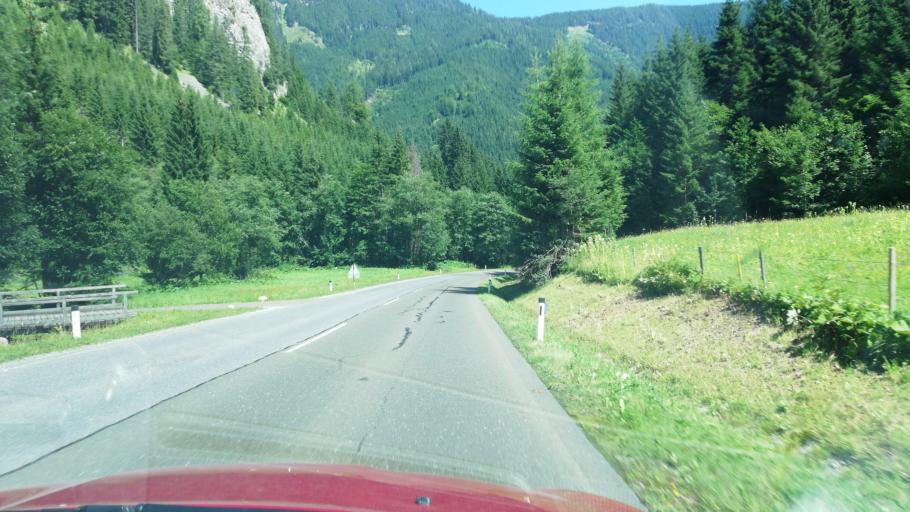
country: AT
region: Styria
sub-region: Politischer Bezirk Murtal
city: Hohentauern
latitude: 47.4422
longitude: 14.5053
